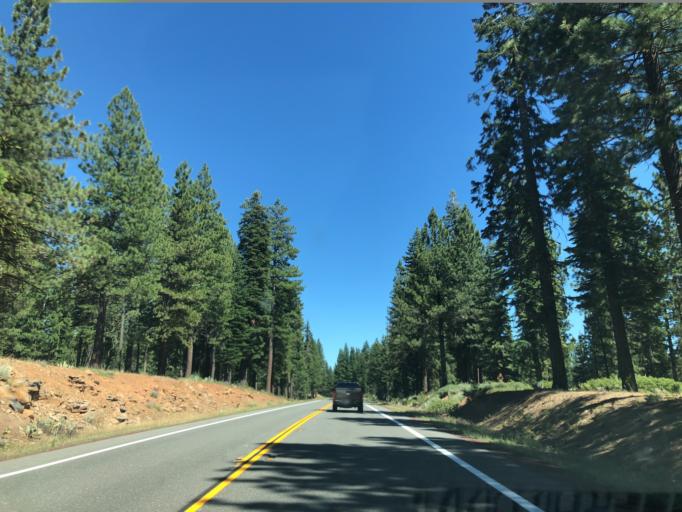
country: US
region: California
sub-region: Lassen County
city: Westwood
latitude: 40.4404
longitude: -120.8572
